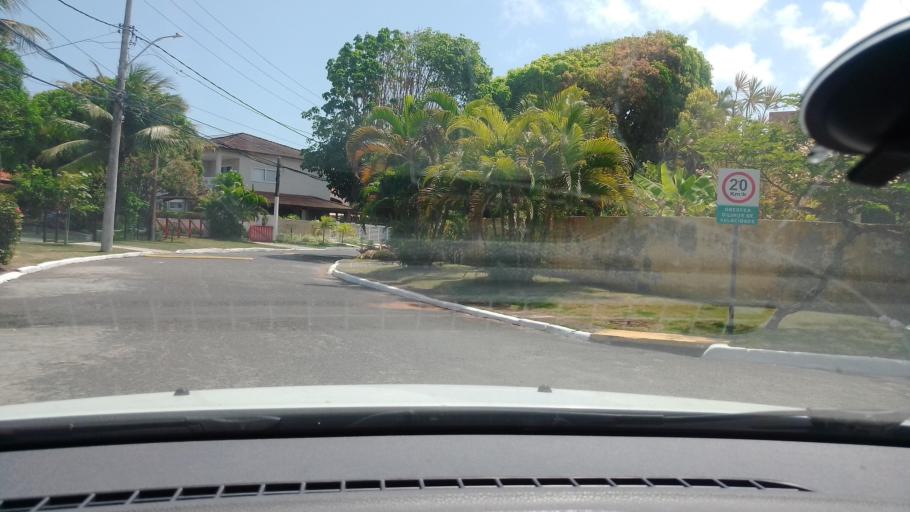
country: BR
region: Bahia
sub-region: Lauro De Freitas
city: Lauro de Freitas
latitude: -12.9540
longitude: -38.3936
